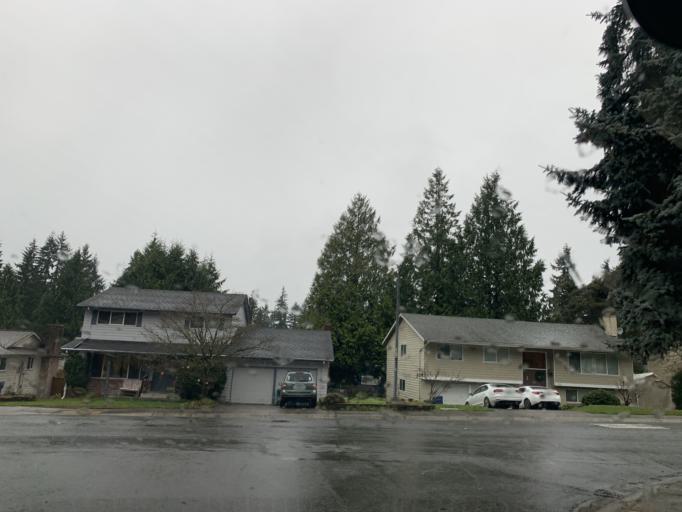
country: US
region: Washington
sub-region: King County
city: Kingsgate
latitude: 47.7376
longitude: -122.1823
